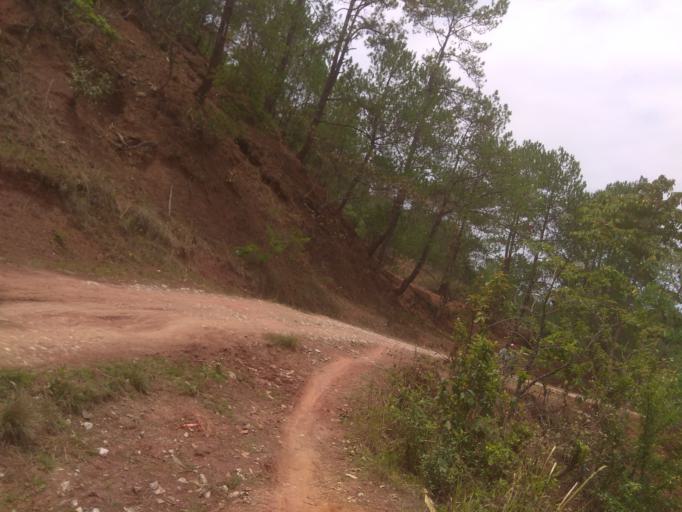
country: MM
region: Mandalay
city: Yamethin
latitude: 20.6083
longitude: 96.5476
